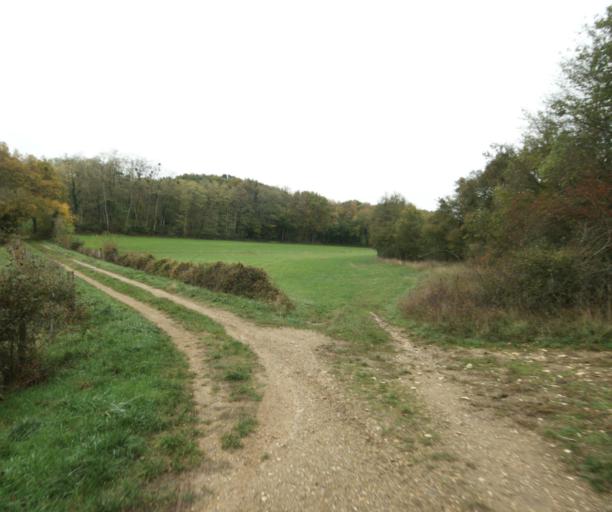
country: FR
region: Bourgogne
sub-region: Departement de Saone-et-Loire
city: Tournus
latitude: 46.4890
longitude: 4.8581
